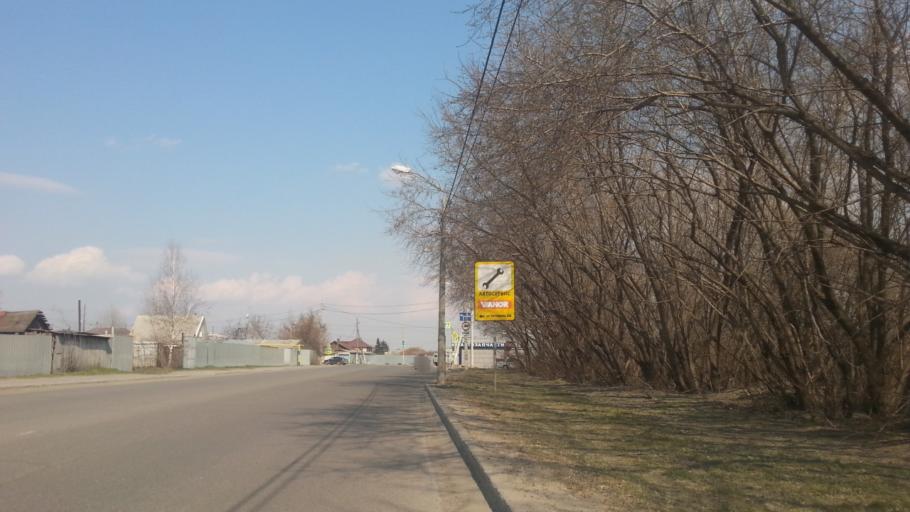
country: RU
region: Altai Krai
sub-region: Gorod Barnaulskiy
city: Barnaul
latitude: 53.3224
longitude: 83.7657
